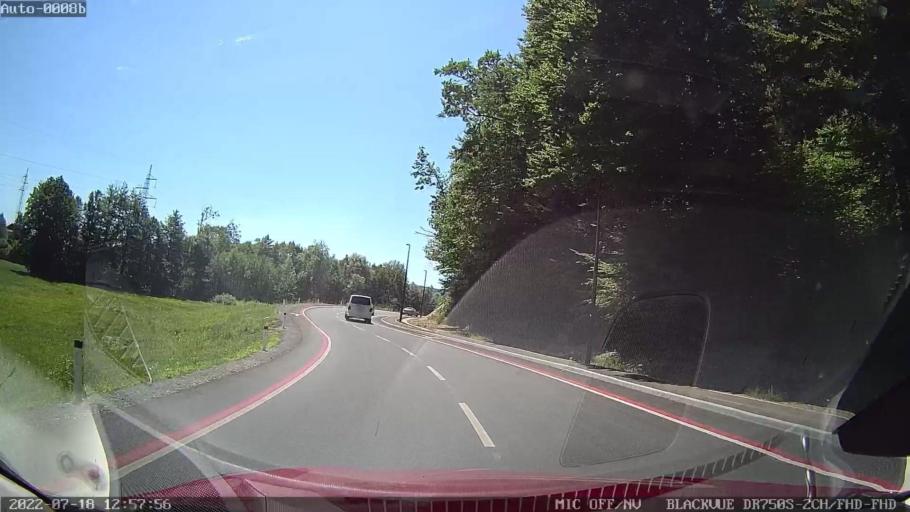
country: SI
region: Dobrova-Horjul-Polhov Gradec
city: Dobrova
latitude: 46.0655
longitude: 14.4202
